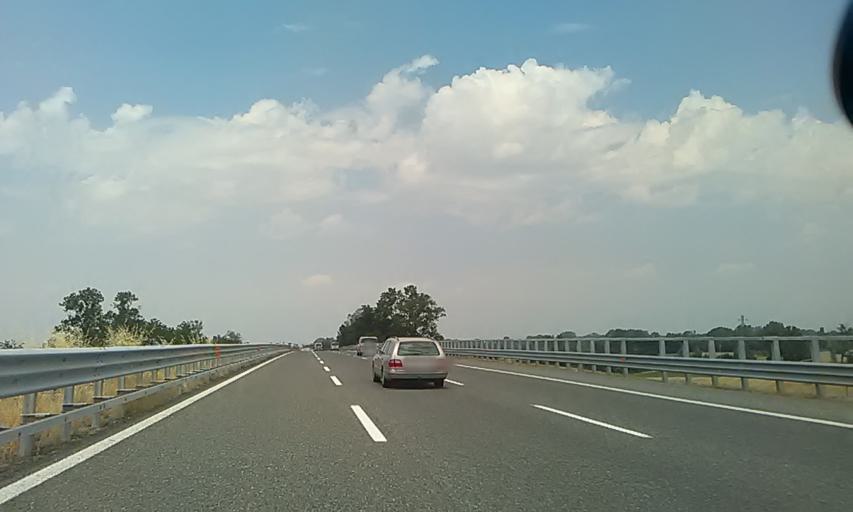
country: IT
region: Piedmont
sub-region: Provincia di Alessandria
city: Castellazzo Bormida
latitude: 44.8495
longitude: 8.5923
